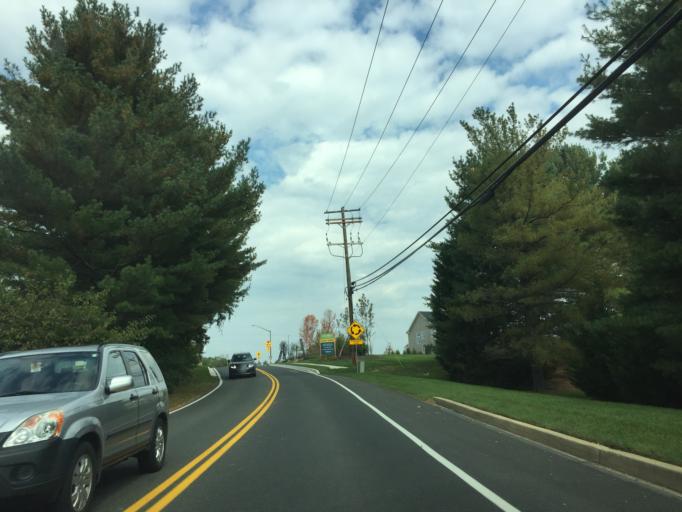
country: US
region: Maryland
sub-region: Harford County
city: Bel Air South
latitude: 39.4819
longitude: -76.2981
